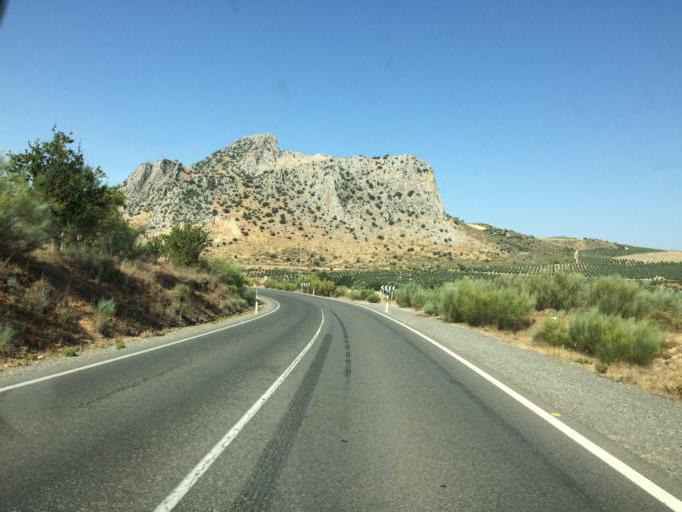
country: ES
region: Andalusia
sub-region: Provincia de Malaga
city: Archidona
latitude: 37.0768
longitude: -4.4739
